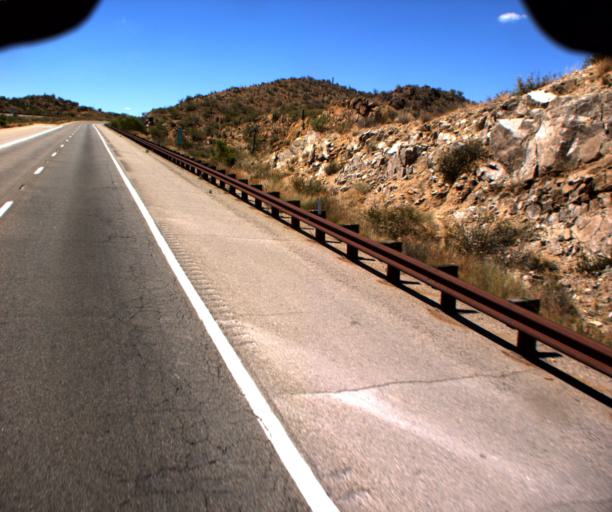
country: US
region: Arizona
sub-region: Yavapai County
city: Bagdad
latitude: 34.4506
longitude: -113.2857
